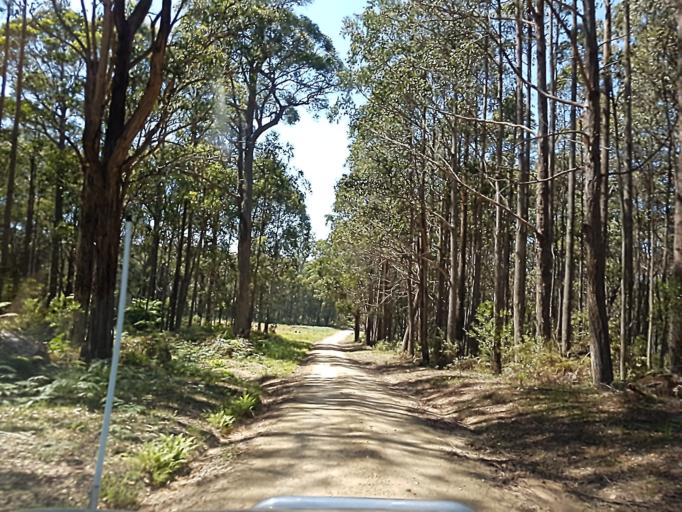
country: AU
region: Victoria
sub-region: East Gippsland
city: Lakes Entrance
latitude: -37.2971
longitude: 148.3220
